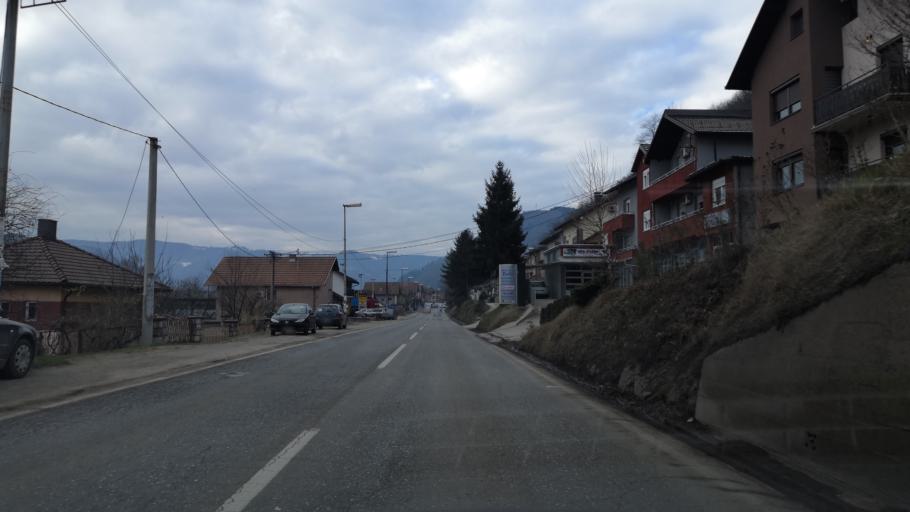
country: BA
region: Republika Srpska
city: Zvornik
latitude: 44.4037
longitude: 19.1169
